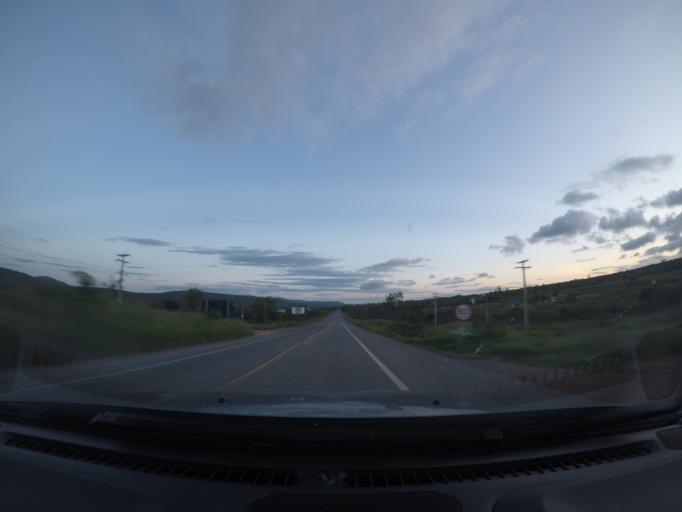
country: BR
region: Bahia
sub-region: Seabra
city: Seabra
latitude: -12.4375
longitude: -41.7551
